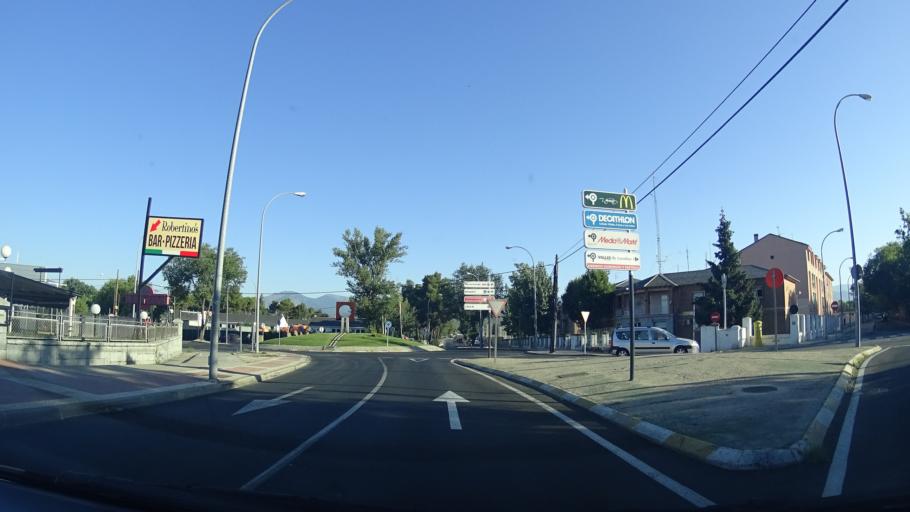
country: ES
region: Madrid
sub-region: Provincia de Madrid
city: Collado-Villalba
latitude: 40.6377
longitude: -4.0037
